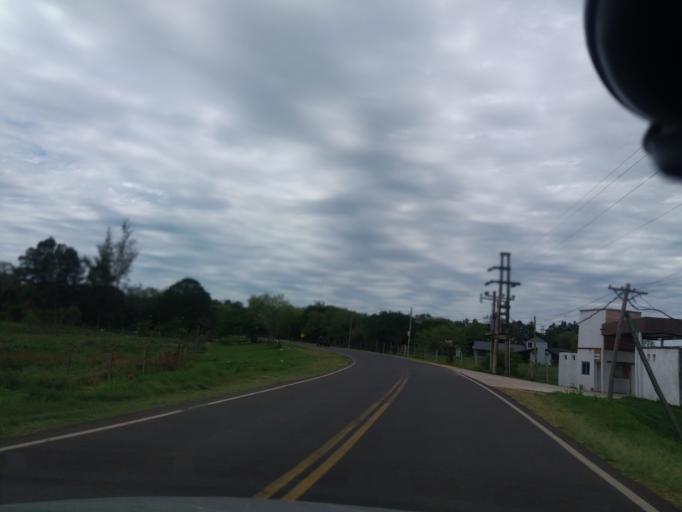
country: AR
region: Corrientes
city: Riachuelo
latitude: -27.4580
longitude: -58.7075
